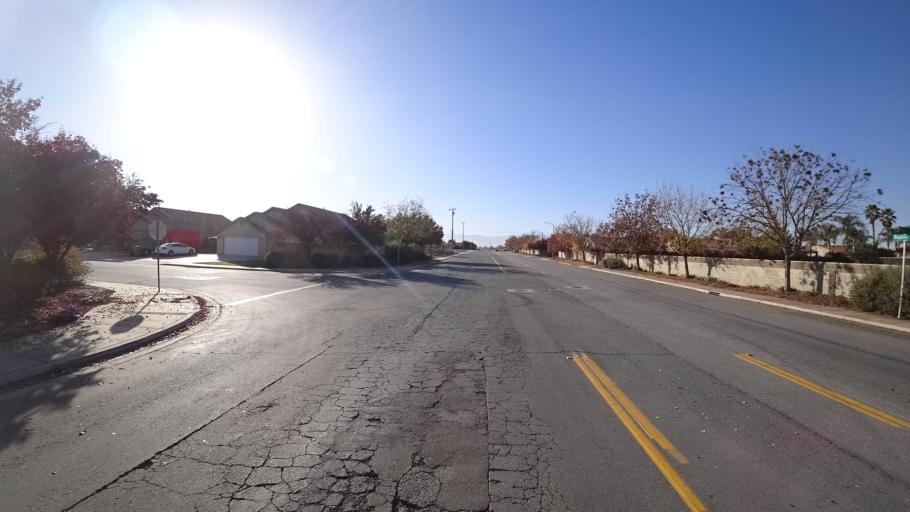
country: US
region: California
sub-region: Kern County
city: Greenfield
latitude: 35.2764
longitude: -119.0301
